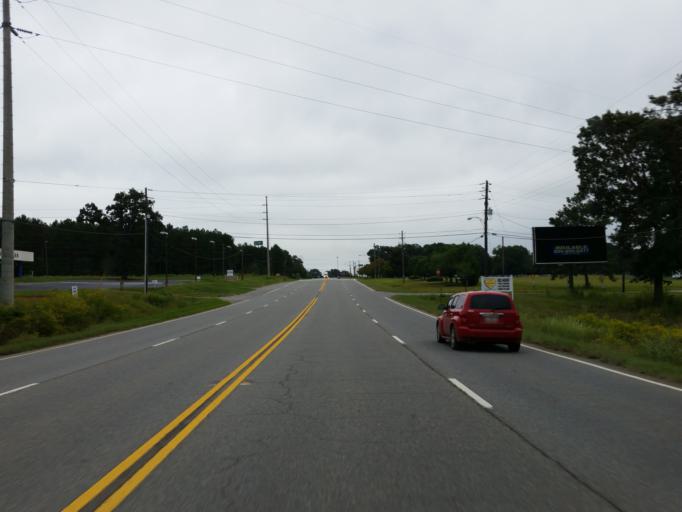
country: US
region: Georgia
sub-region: Houston County
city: Perry
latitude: 32.4773
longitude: -83.7515
